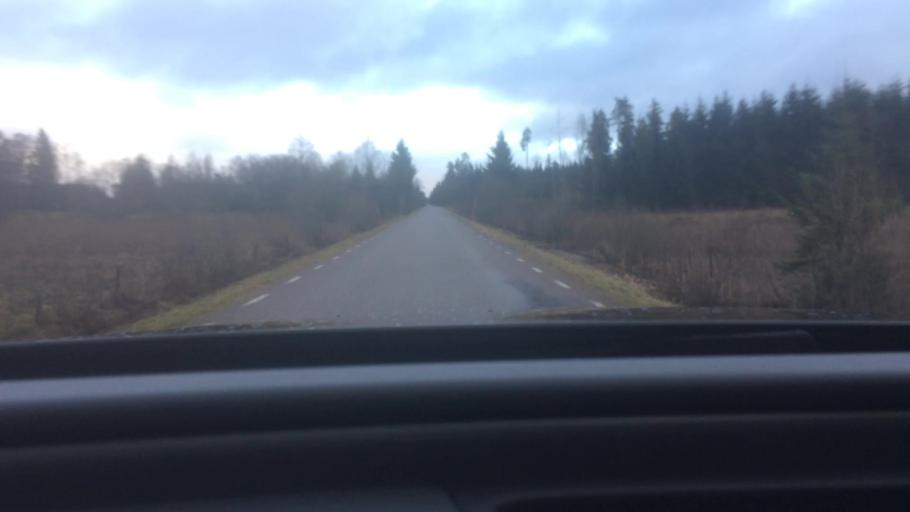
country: SE
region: Vaestra Goetaland
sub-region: Falkopings Kommun
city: Falkoeping
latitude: 57.9994
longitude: 13.4830
